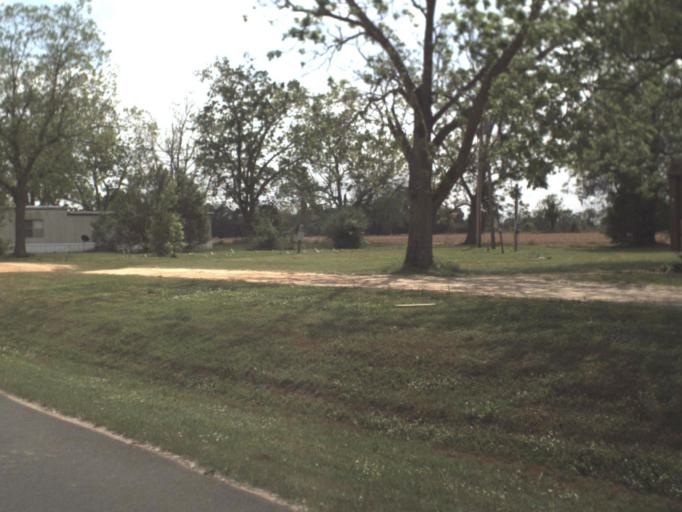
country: US
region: Florida
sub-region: Escambia County
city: Century
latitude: 30.9369
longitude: -87.1568
